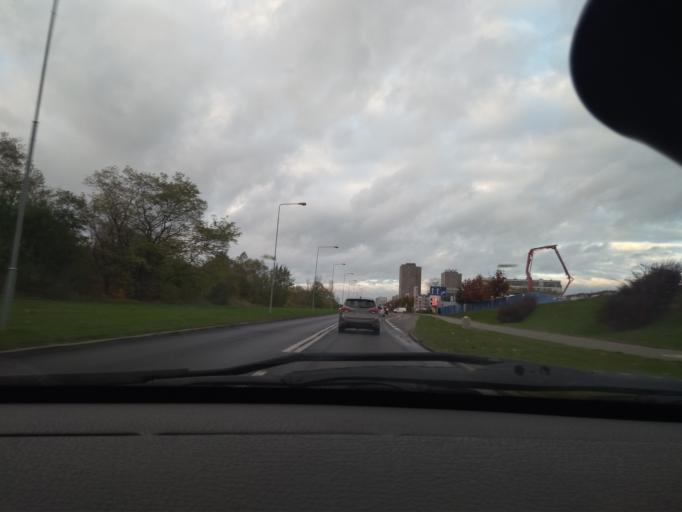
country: PL
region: Greater Poland Voivodeship
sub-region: Poznan
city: Poznan
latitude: 52.4438
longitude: 16.9206
